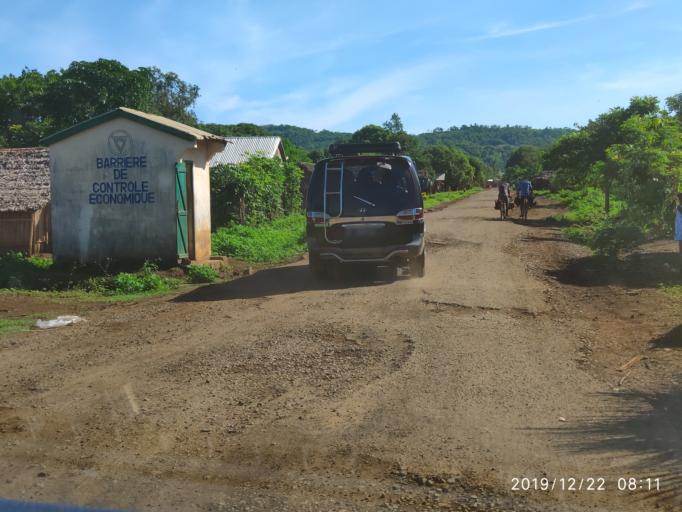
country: MG
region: Diana
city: Ambilobe
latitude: -12.9243
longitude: 49.1680
